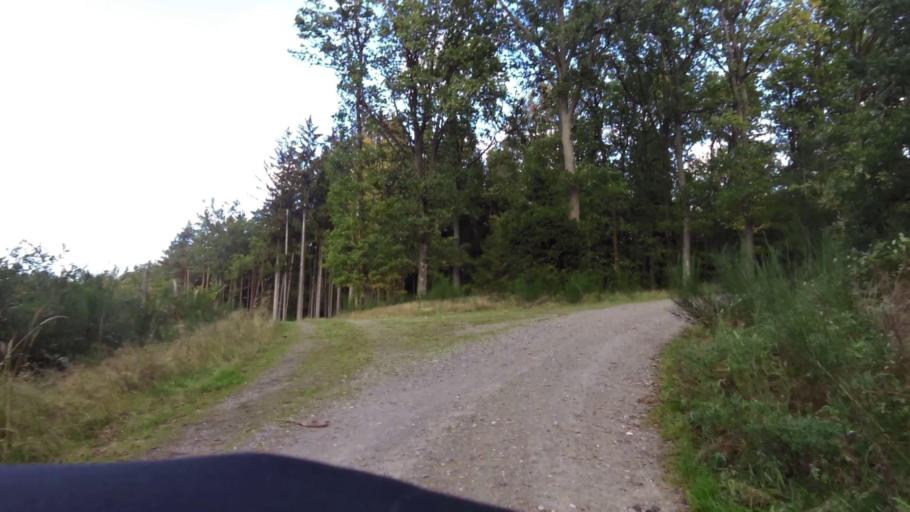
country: PL
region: West Pomeranian Voivodeship
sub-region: Powiat bialogardzki
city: Bialogard
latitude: 54.0407
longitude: 16.1298
